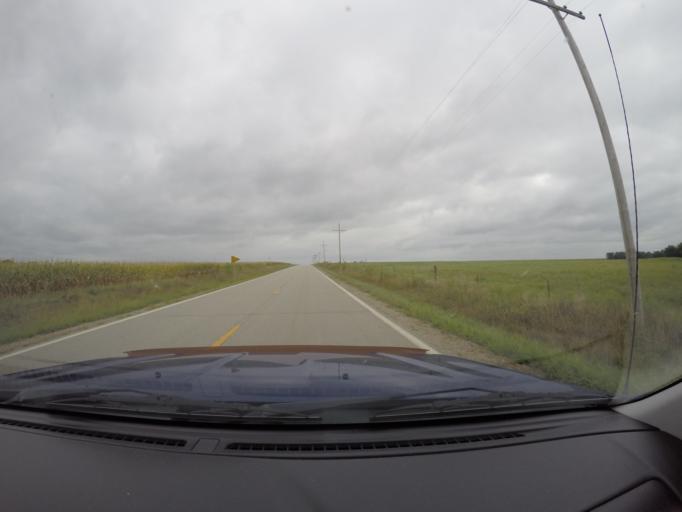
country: US
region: Kansas
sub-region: Morris County
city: Council Grove
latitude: 38.8298
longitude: -96.5941
